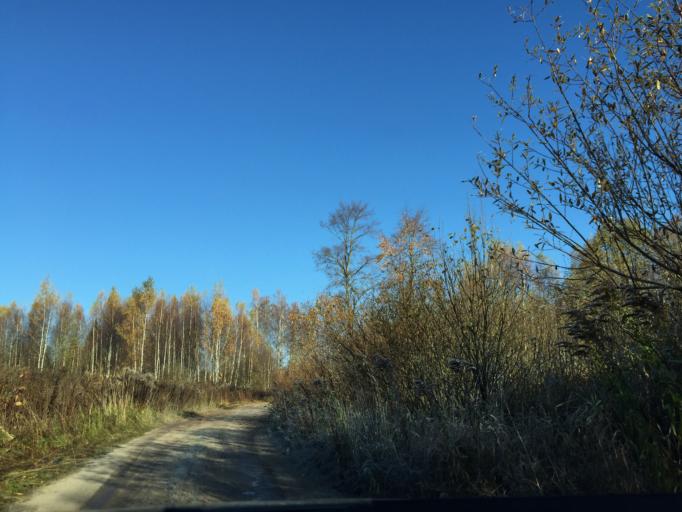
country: LV
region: Aizkraukles Rajons
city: Aizkraukle
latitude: 56.7098
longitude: 25.2999
